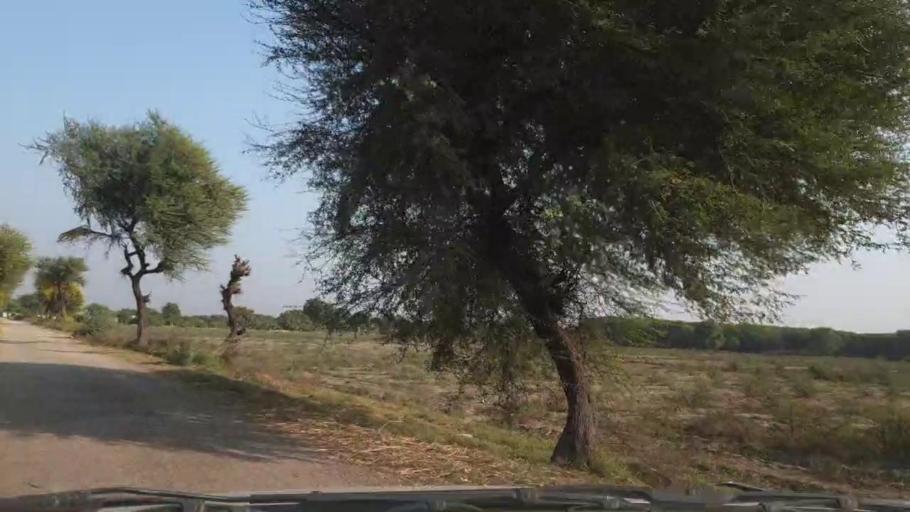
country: PK
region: Sindh
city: Chambar
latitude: 25.2145
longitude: 68.6858
